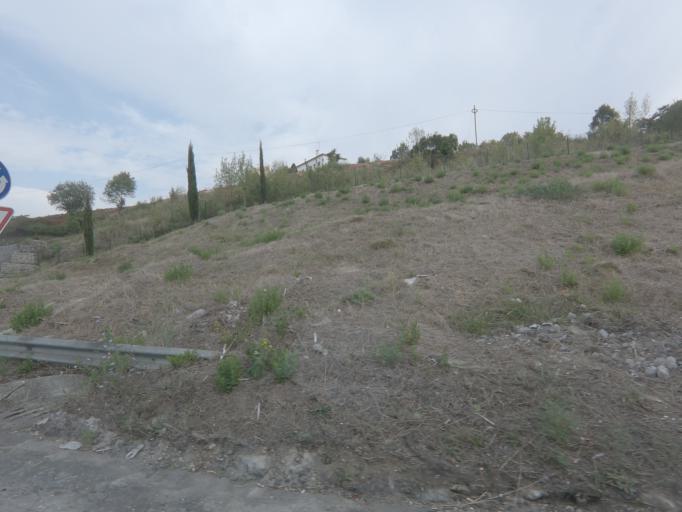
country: PT
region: Coimbra
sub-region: Coimbra
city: Coimbra
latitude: 40.2138
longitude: -8.4459
